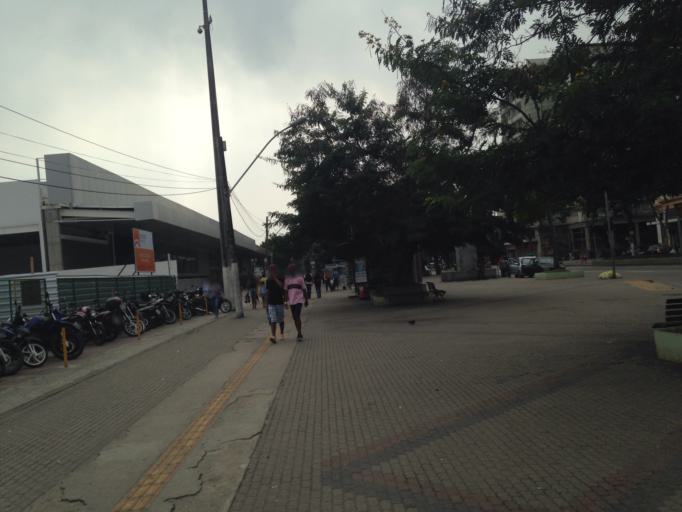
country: BR
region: Rio de Janeiro
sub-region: Niteroi
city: Niteroi
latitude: -22.8944
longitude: -43.1241
